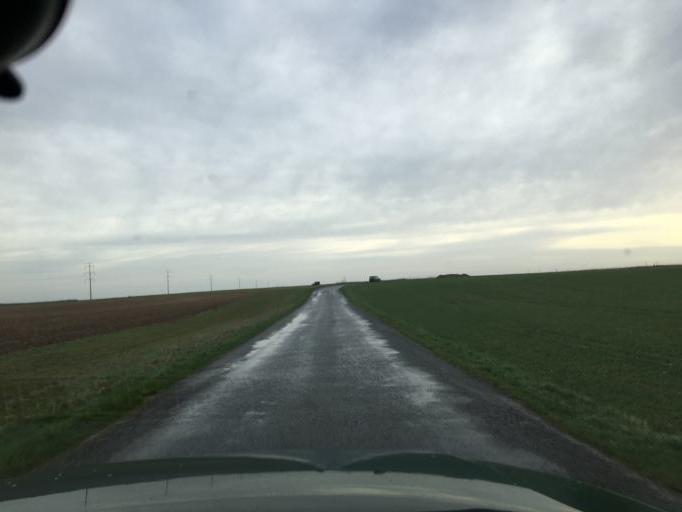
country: FR
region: Centre
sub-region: Departement du Loiret
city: Beaugency
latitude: 47.8135
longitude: 1.6145
